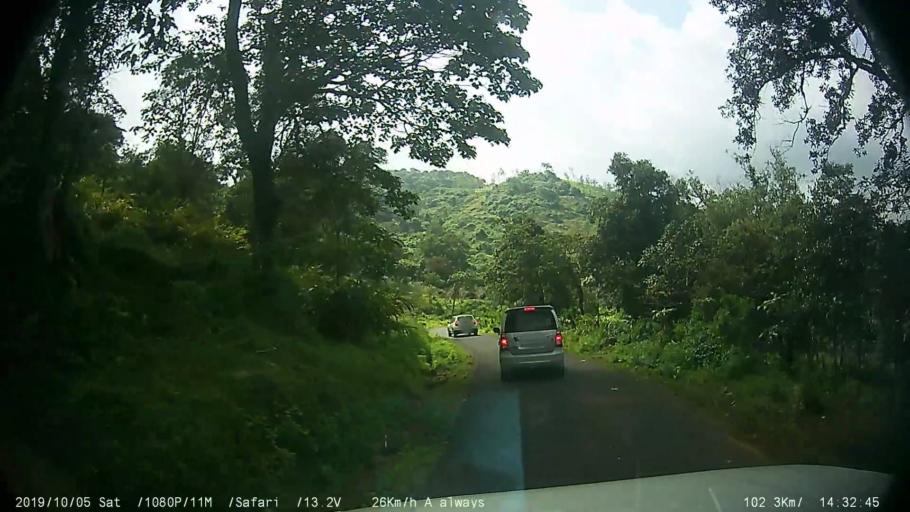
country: IN
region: Kerala
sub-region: Kottayam
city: Erattupetta
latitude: 9.6135
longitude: 76.9686
